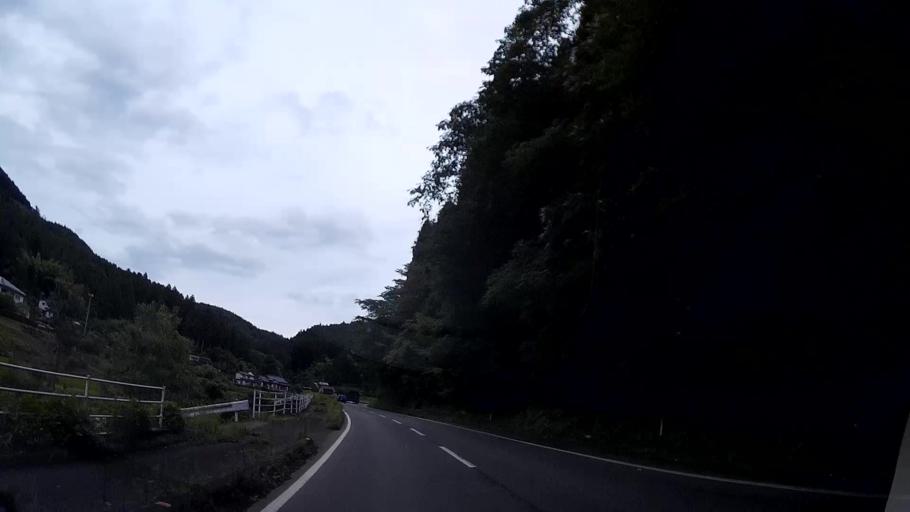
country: JP
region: Oita
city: Hita
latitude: 33.1263
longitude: 131.0005
